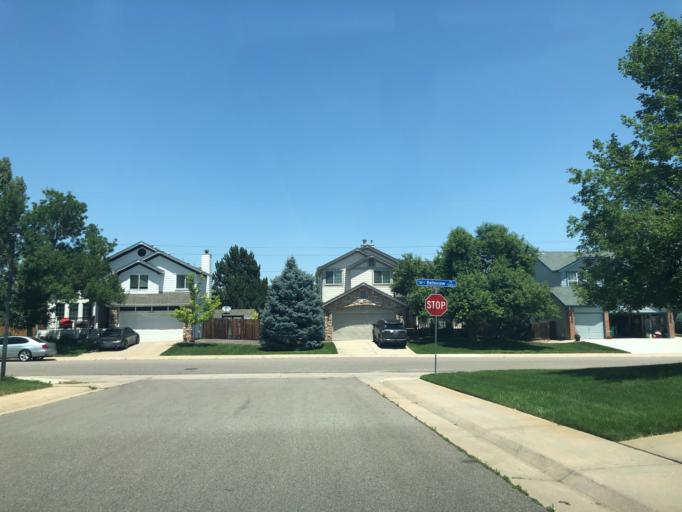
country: US
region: Colorado
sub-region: Arapahoe County
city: Dove Valley
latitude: 39.6233
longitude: -104.7577
